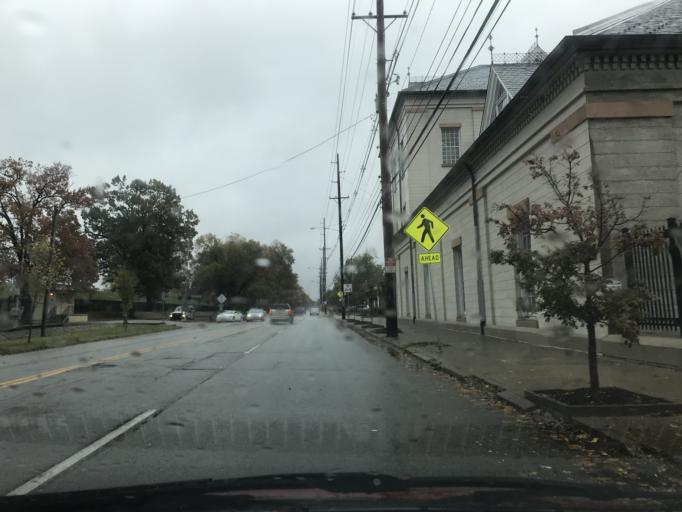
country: US
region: Kentucky
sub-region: Jefferson County
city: Saint Matthews
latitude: 38.2545
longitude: -85.6815
